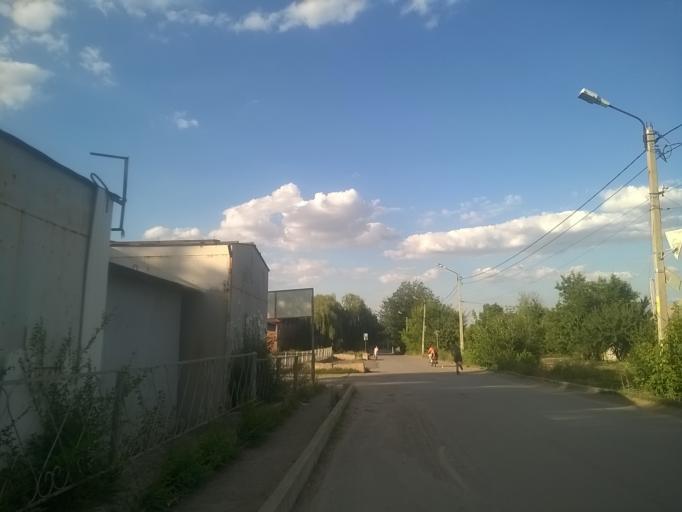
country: RU
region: Rostov
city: Donetsk
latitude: 48.3357
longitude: 39.9528
